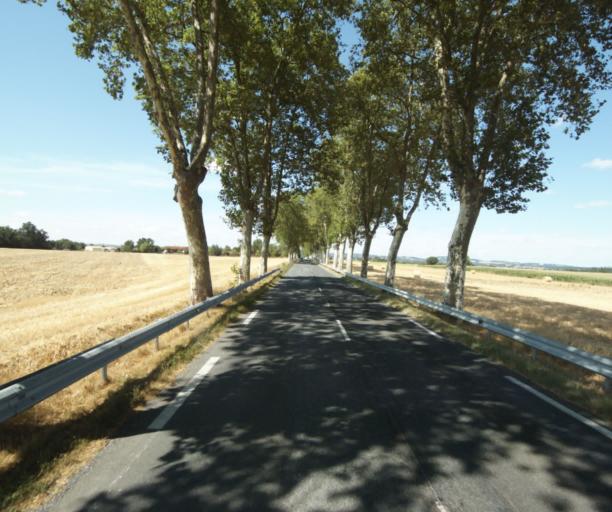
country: FR
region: Midi-Pyrenees
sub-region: Departement de la Haute-Garonne
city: Revel
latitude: 43.4925
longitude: 2.0130
